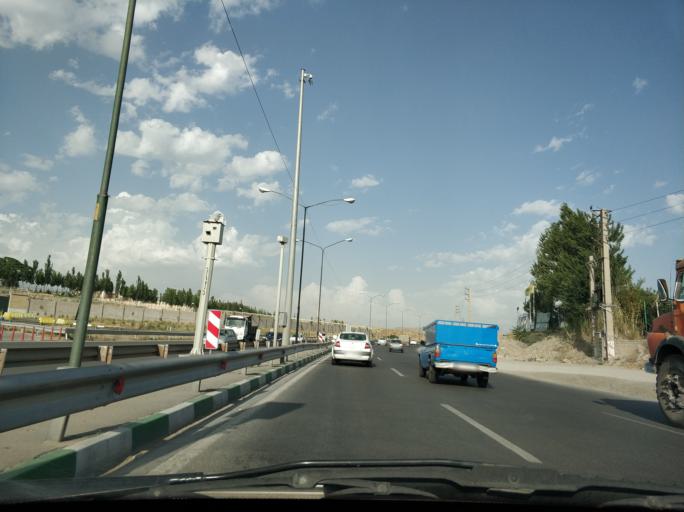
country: IR
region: Tehran
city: Tajrish
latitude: 35.7482
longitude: 51.5919
